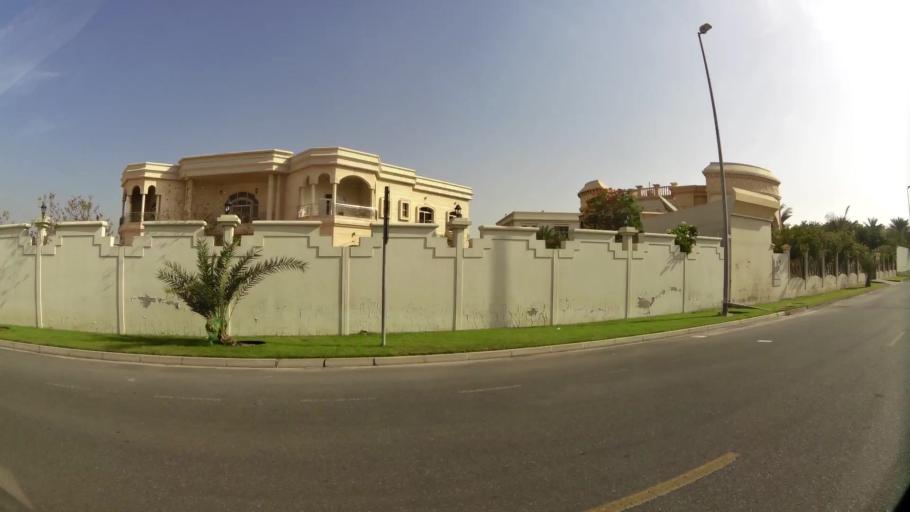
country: AE
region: Ash Shariqah
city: Sharjah
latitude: 25.2423
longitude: 55.4090
